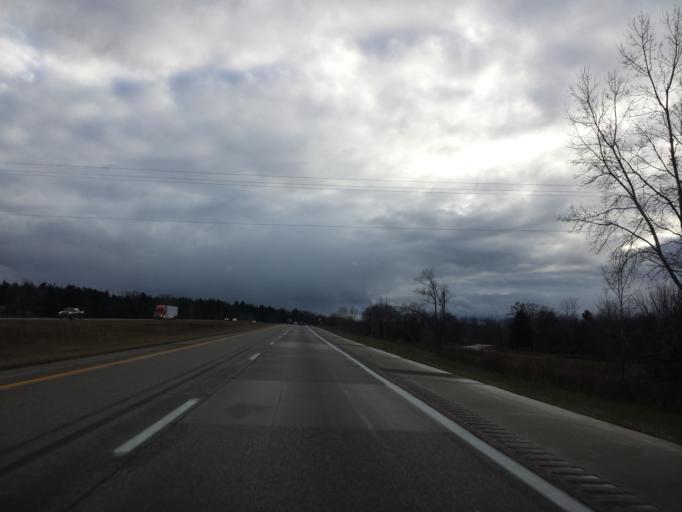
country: US
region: Michigan
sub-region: Shiawassee County
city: Perry
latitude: 42.8231
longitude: -84.2672
